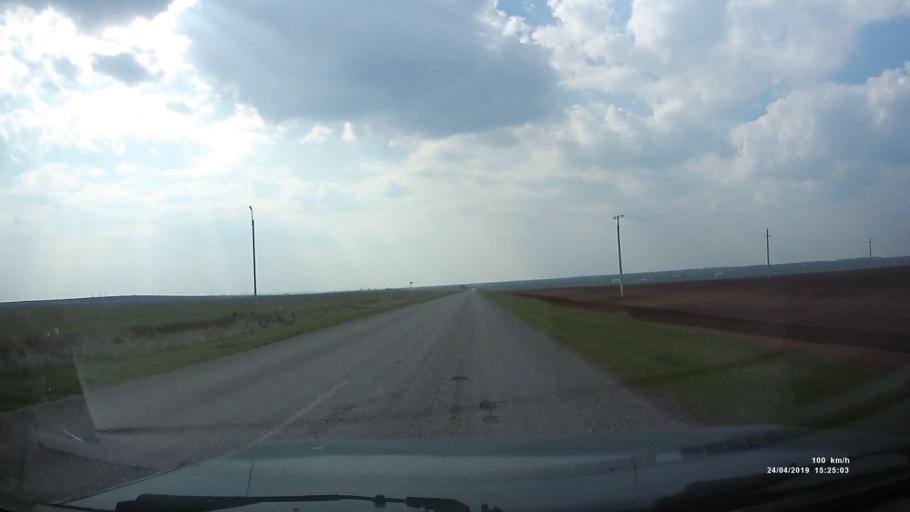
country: RU
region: Rostov
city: Remontnoye
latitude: 46.5506
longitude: 43.0560
